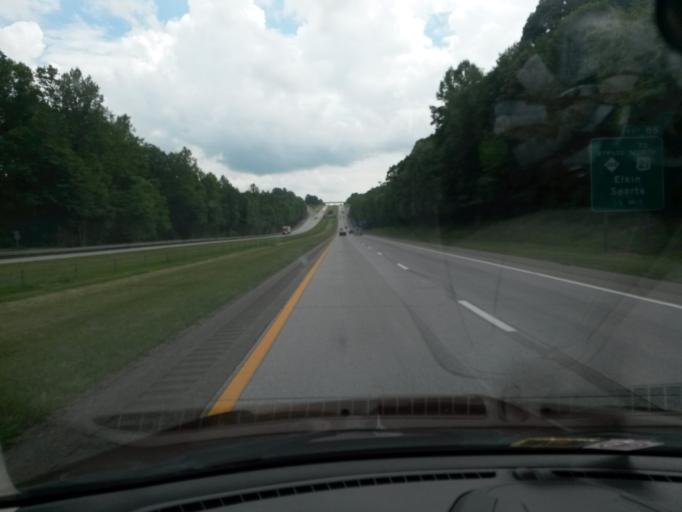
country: US
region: North Carolina
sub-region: Surry County
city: Elkin
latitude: 36.2916
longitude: -80.8154
